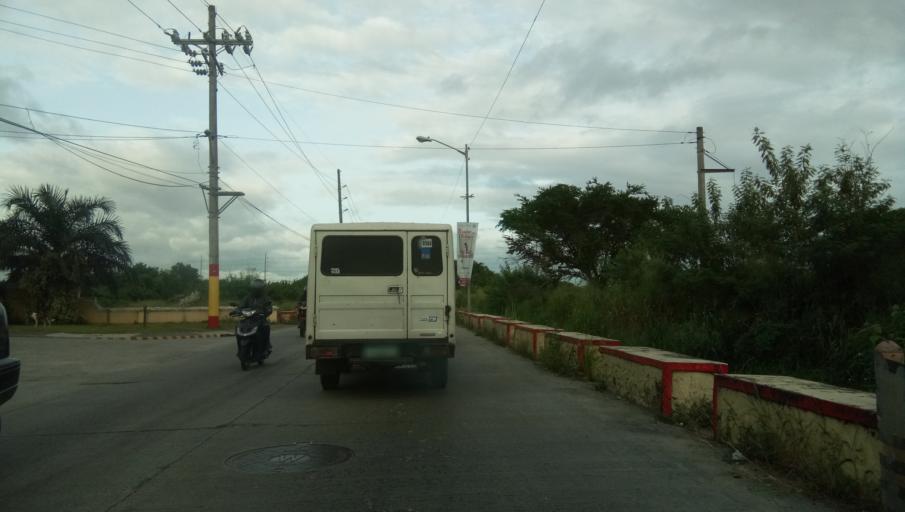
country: PH
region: Calabarzon
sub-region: Province of Cavite
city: Dasmarinas
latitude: 14.3678
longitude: 120.9332
